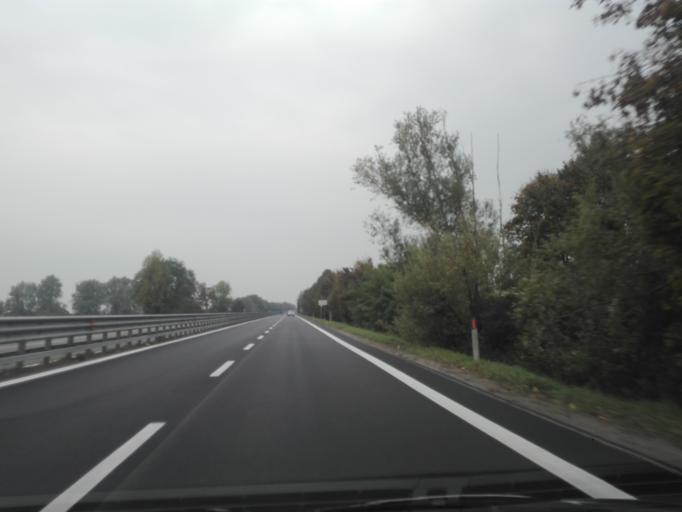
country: IT
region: Veneto
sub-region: Provincia di Verona
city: Villa Bartolomea
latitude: 45.1610
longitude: 11.3101
